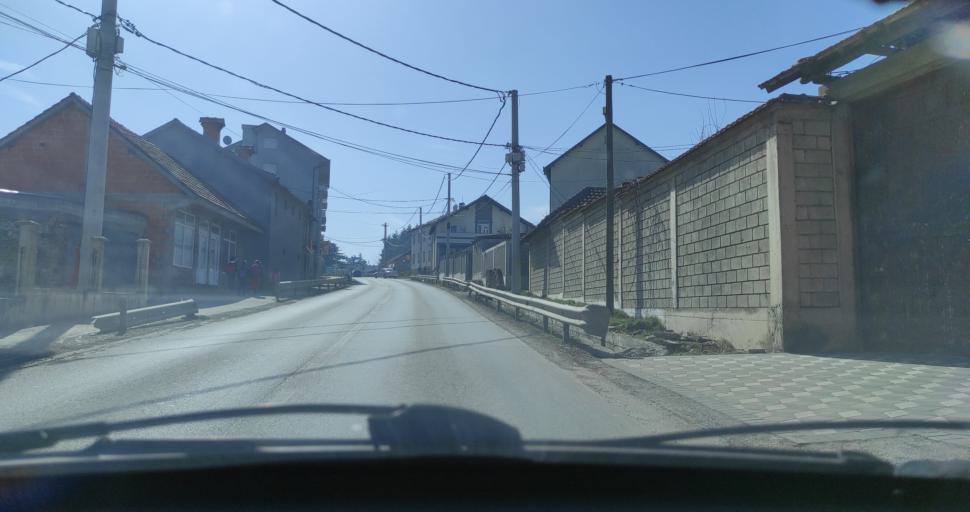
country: XK
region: Gjakova
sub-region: Komuna e Decanit
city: Strellc i Eperm
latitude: 42.5803
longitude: 20.2945
